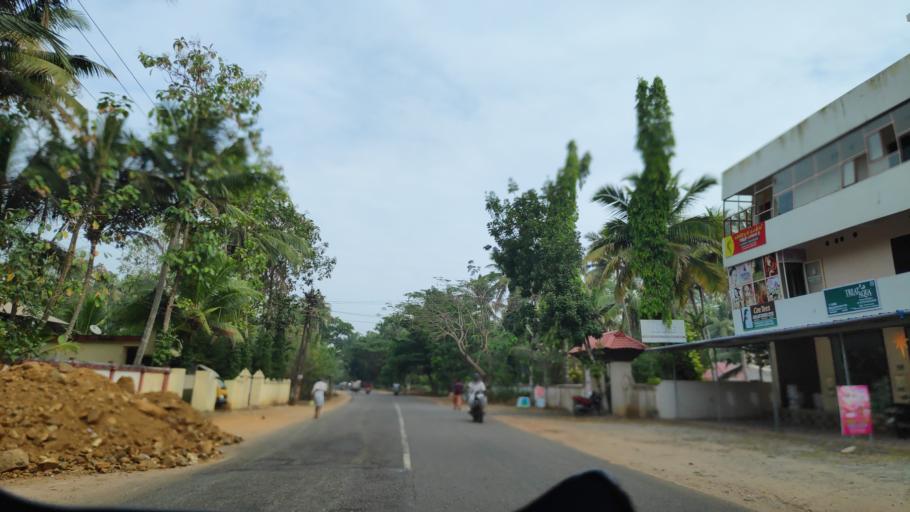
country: IN
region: Kerala
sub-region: Kottayam
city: Vaikam
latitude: 9.7408
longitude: 76.3628
